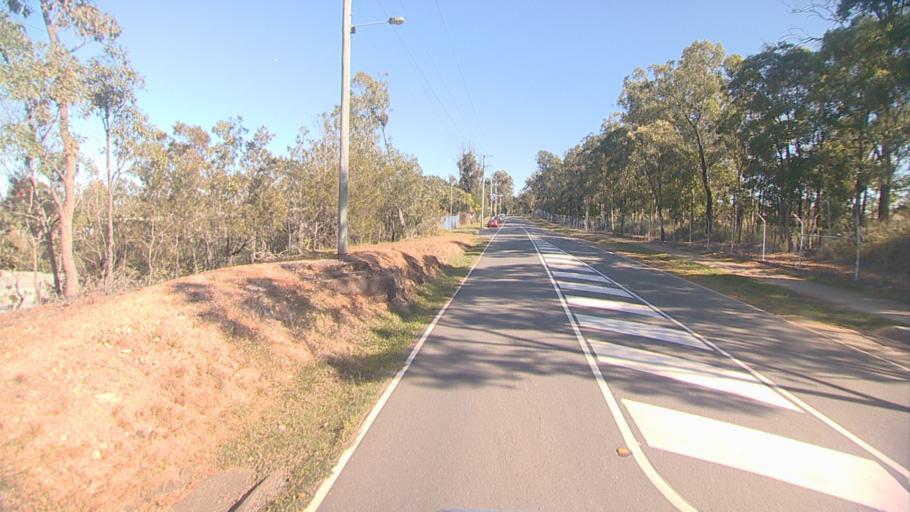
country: AU
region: Queensland
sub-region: Logan
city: Logan City
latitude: -27.6642
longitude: 153.1147
